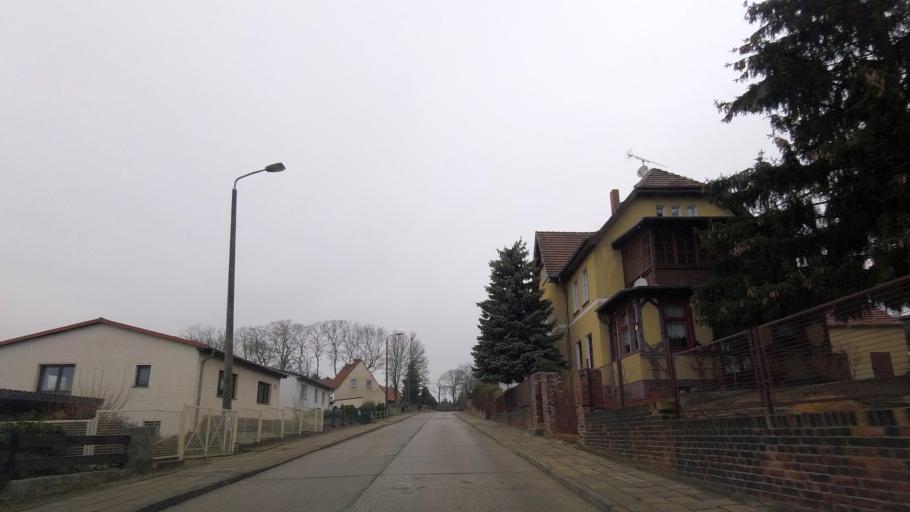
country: DE
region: Brandenburg
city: Juterbog
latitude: 52.0006
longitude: 13.0788
